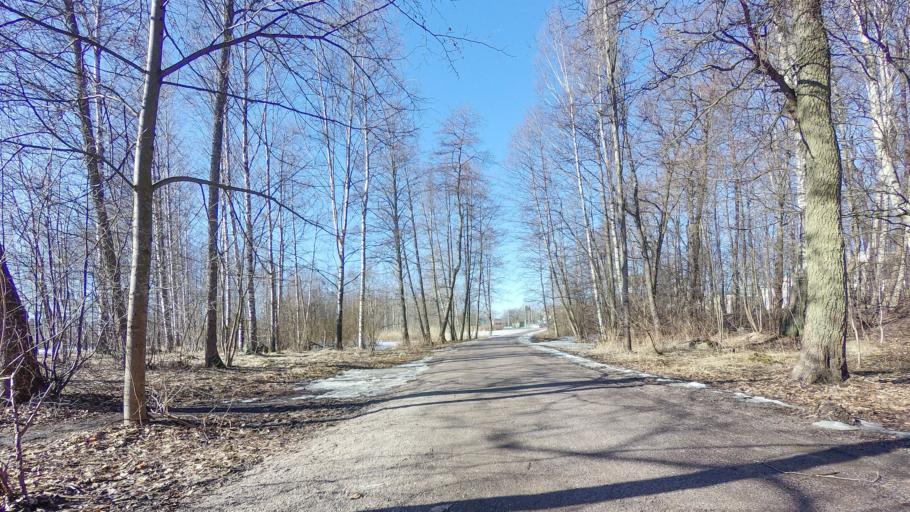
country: FI
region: Uusimaa
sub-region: Helsinki
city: Vantaa
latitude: 60.1939
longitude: 25.0584
